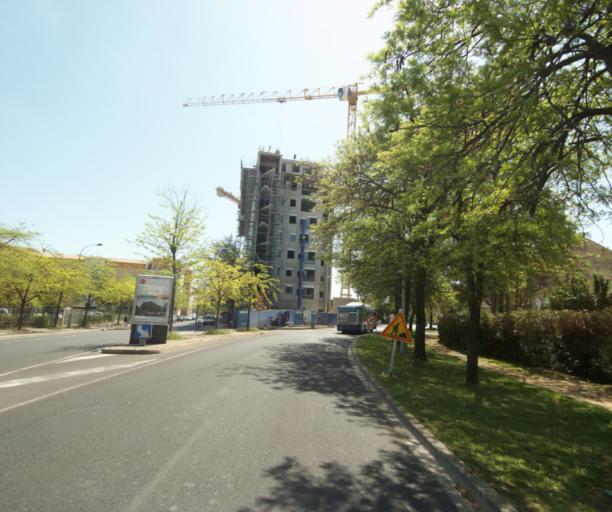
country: FR
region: Languedoc-Roussillon
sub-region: Departement de l'Herault
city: Montpellier
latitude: 43.6023
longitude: 3.8915
